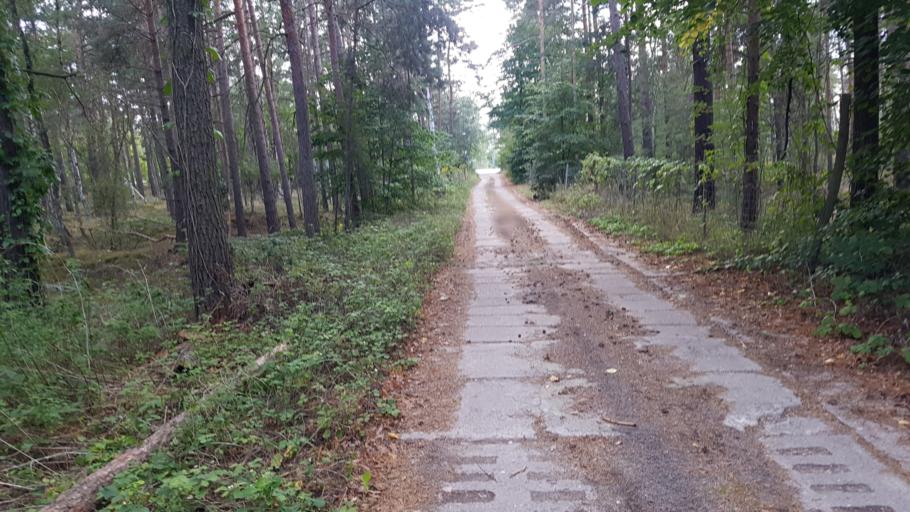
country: DE
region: Brandenburg
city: Sonnewalde
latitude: 51.6355
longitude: 13.6482
